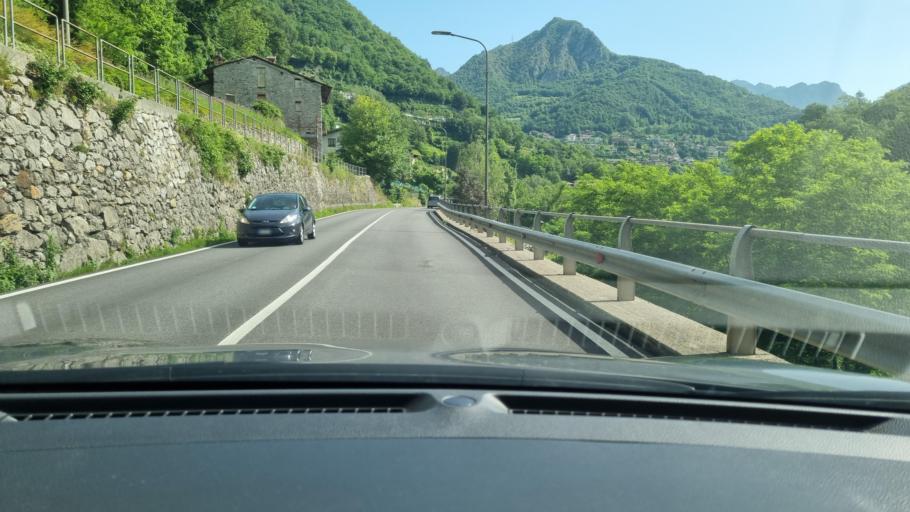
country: IT
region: Lombardy
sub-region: Provincia di Bergamo
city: Zogno
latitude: 45.8016
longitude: 9.6702
